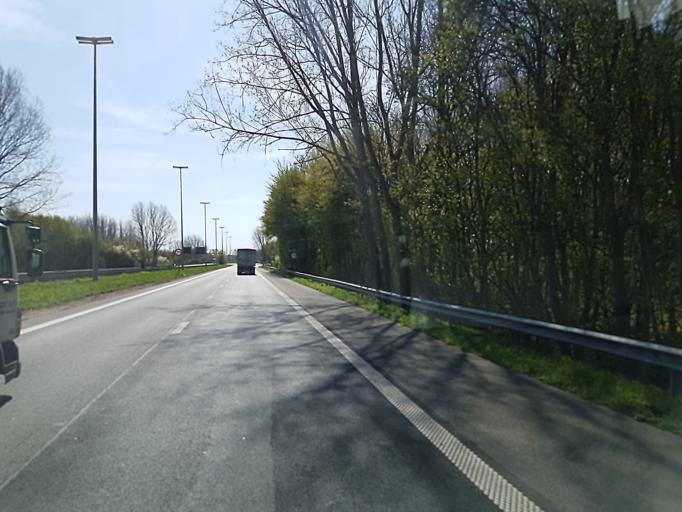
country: BE
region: Wallonia
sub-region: Province du Hainaut
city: Rumes
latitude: 50.6168
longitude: 3.3221
